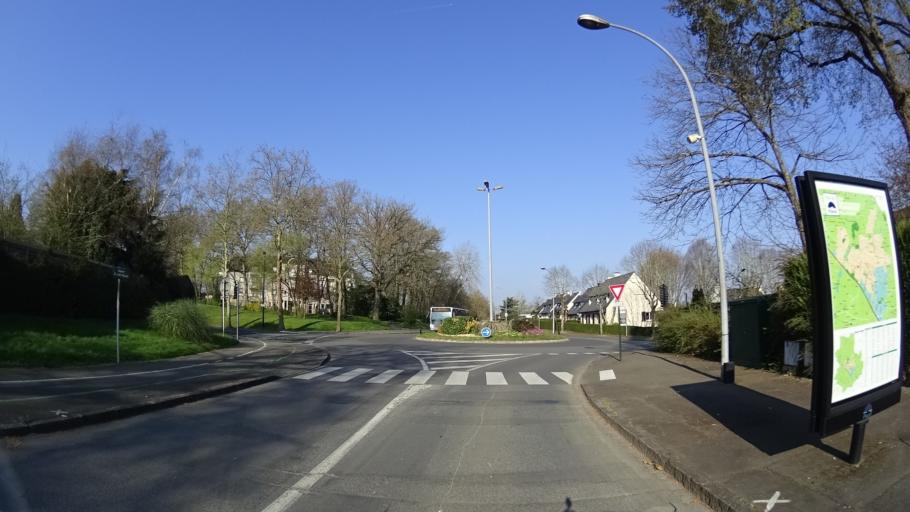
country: FR
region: Brittany
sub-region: Departement d'Ille-et-Vilaine
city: Pace
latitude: 48.1478
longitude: -1.7805
